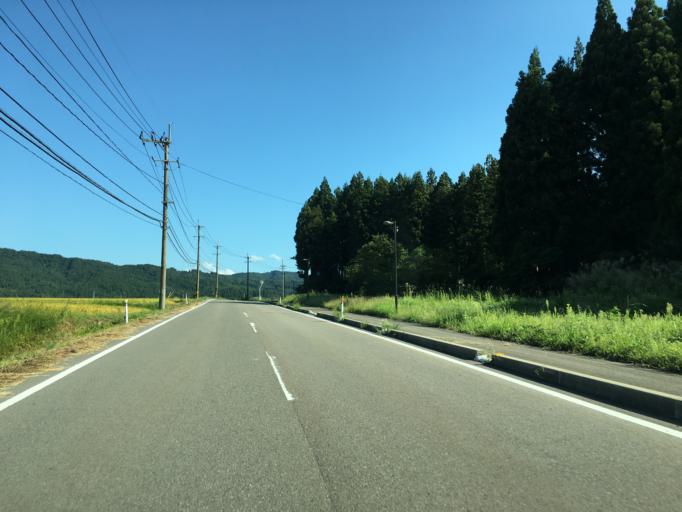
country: JP
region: Fukushima
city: Kitakata
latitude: 37.5938
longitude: 139.6544
